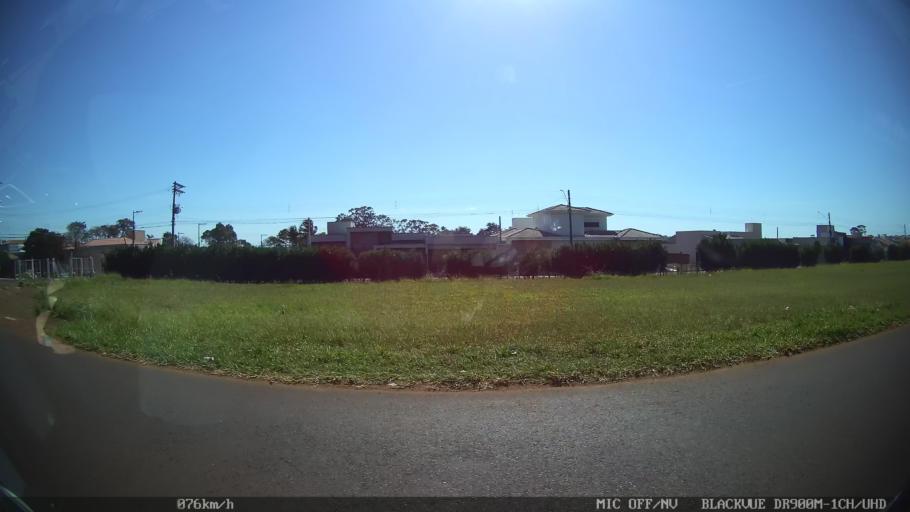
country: BR
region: Sao Paulo
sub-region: Batatais
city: Batatais
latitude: -20.8749
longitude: -47.5896
